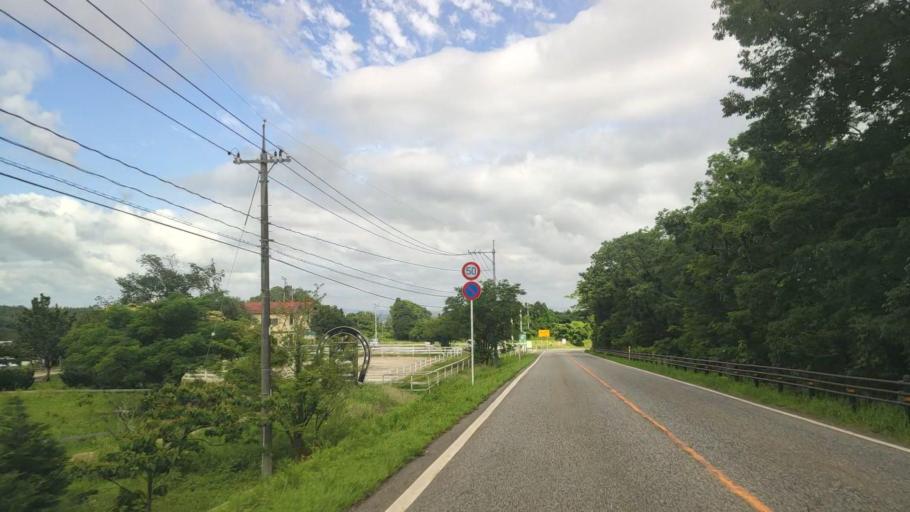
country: JP
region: Tottori
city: Yonago
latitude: 35.4137
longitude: 133.4670
